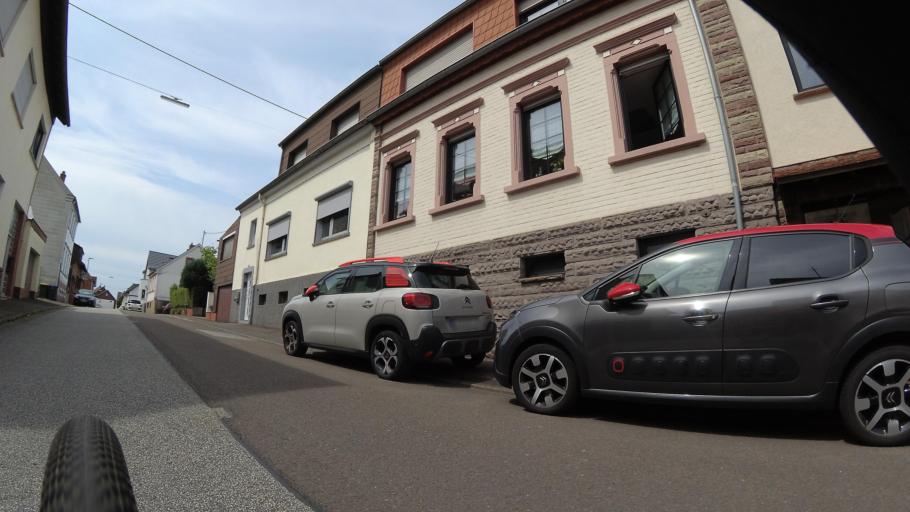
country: DE
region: Saarland
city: Merchweiler
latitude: 49.3354
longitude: 7.0572
